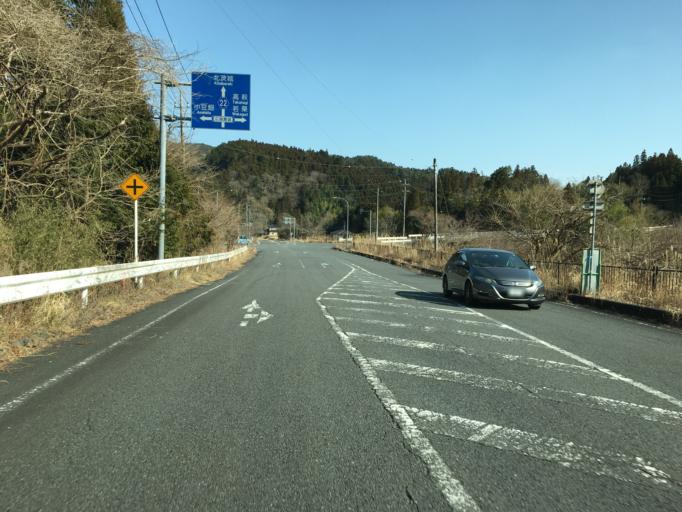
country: JP
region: Ibaraki
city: Kitaibaraki
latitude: 36.7966
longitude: 140.6474
